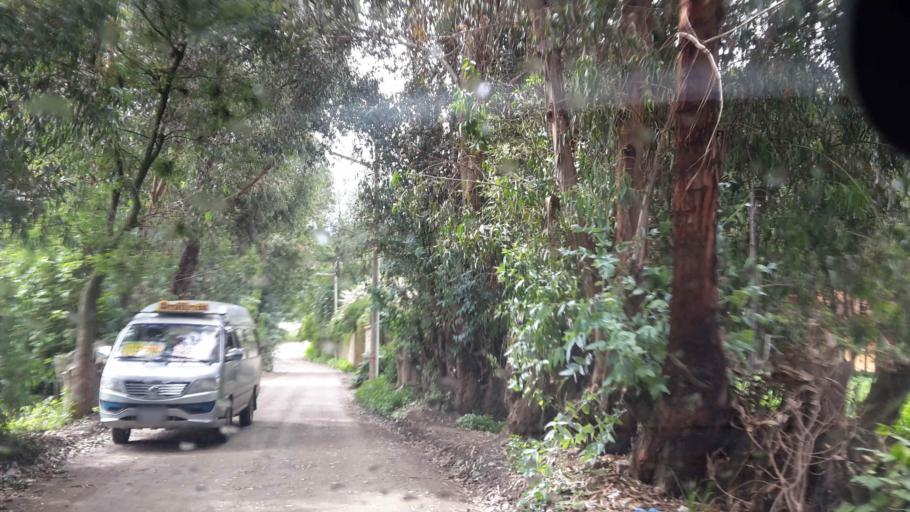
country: BO
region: Cochabamba
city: Cochabamba
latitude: -17.3594
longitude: -66.2163
